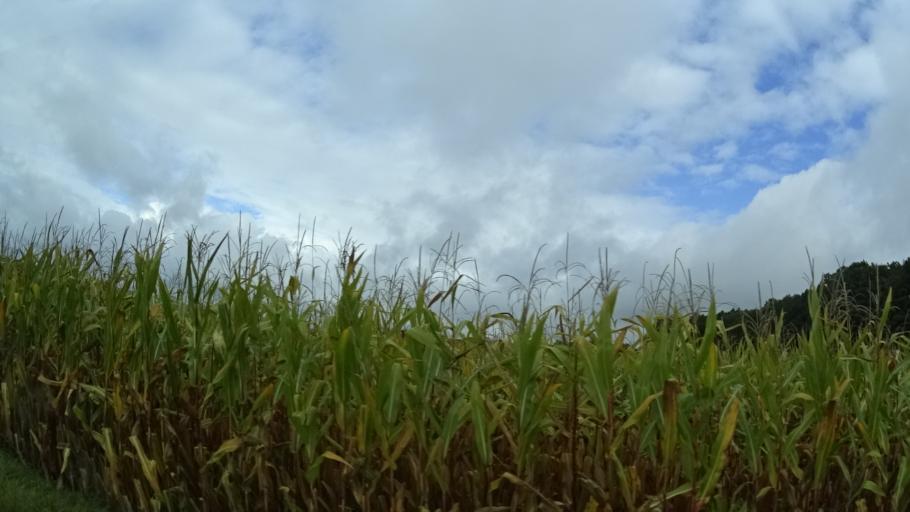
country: DE
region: Bavaria
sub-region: Upper Franconia
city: Schesslitz
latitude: 50.0179
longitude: 11.0106
